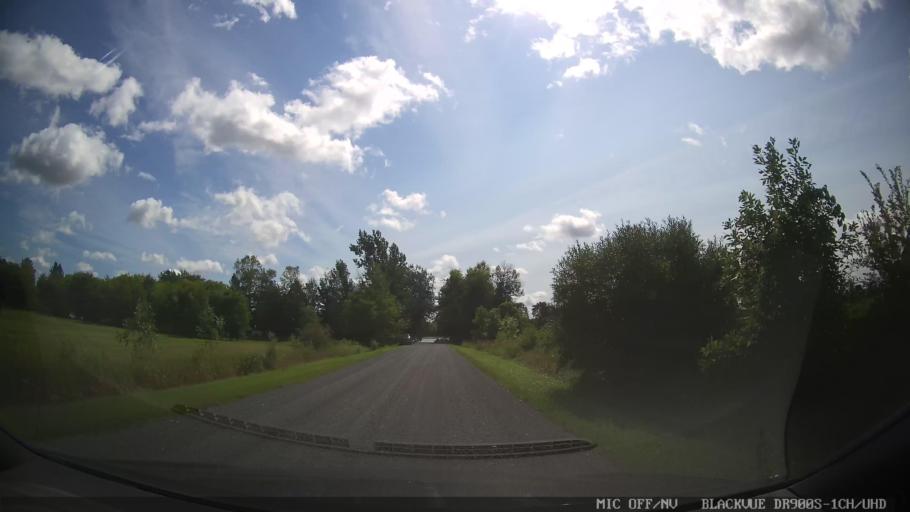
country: CA
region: Ontario
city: Bells Corners
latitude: 45.0422
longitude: -75.6959
